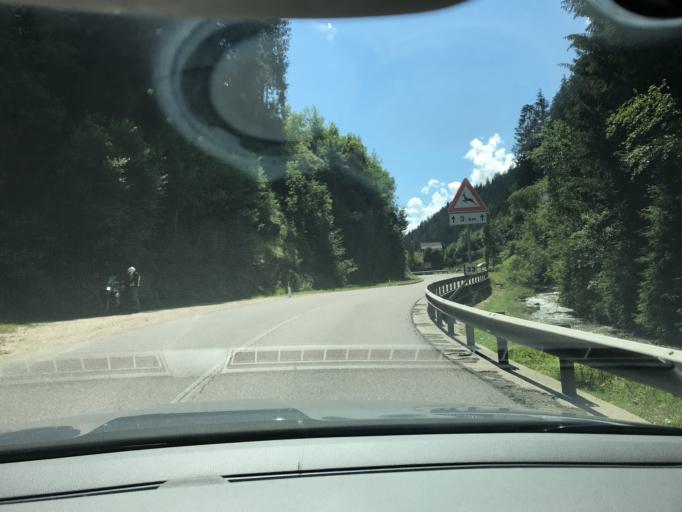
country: IT
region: Trentino-Alto Adige
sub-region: Bolzano
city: San Vigilio
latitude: 46.7176
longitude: 11.9022
